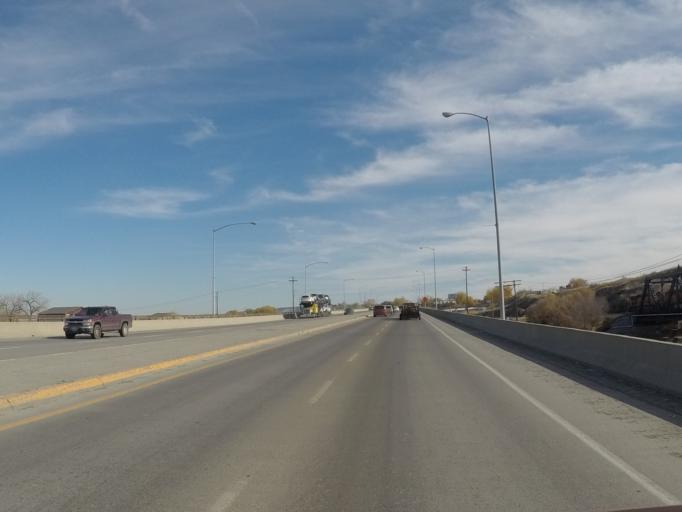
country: US
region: Montana
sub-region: Yellowstone County
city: Billings
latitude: 45.7965
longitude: -108.4710
